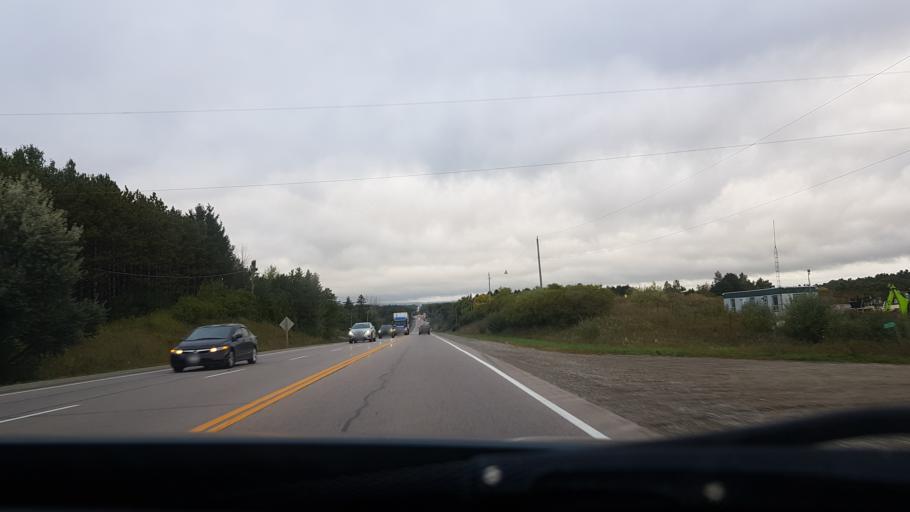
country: CA
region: Ontario
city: Bradford West Gwillimbury
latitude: 43.9893
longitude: -79.7780
